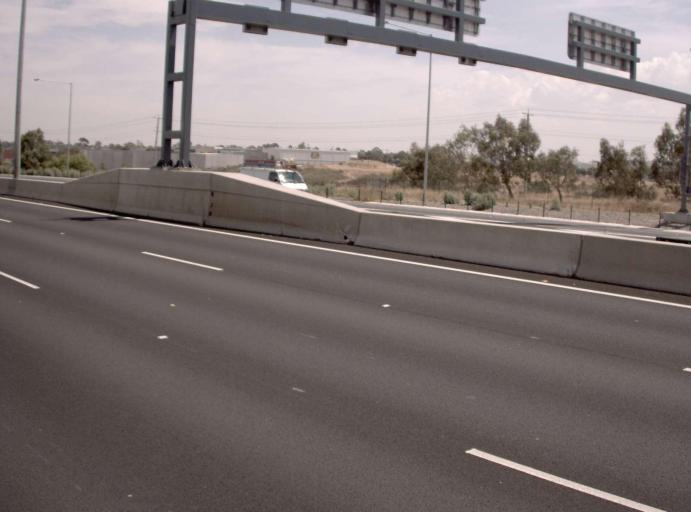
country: AU
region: Victoria
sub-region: Moonee Valley
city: Airport West
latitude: -37.7185
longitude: 144.8721
